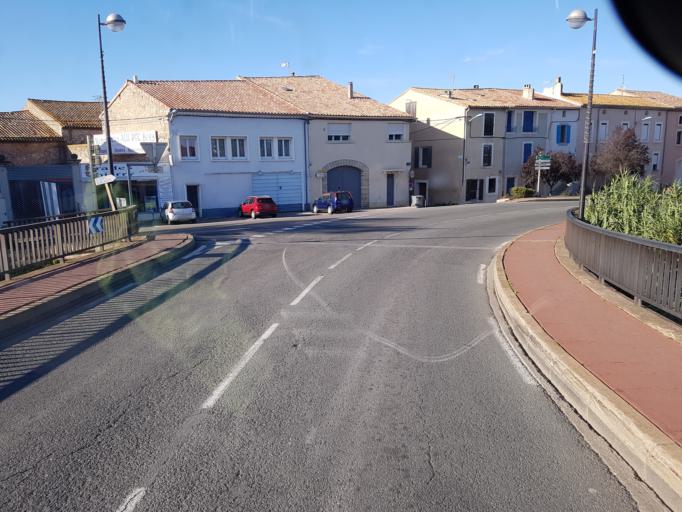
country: FR
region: Languedoc-Roussillon
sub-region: Departement de l'Aude
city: Coursan
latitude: 43.2359
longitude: 3.0571
